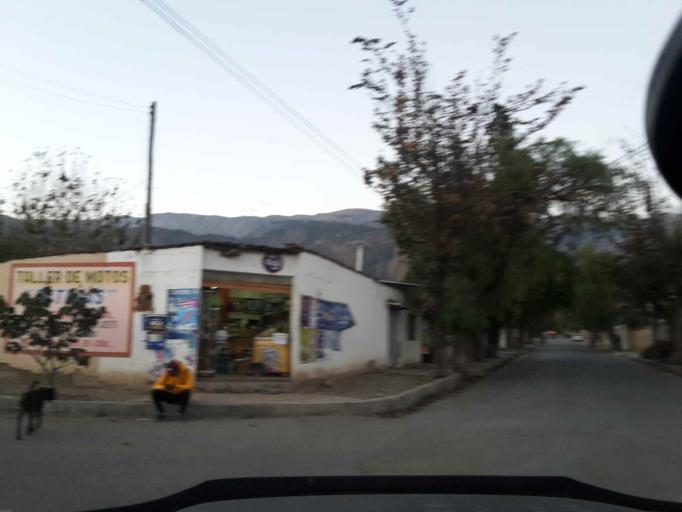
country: BO
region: Cochabamba
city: Cochabamba
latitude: -17.3361
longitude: -66.2175
